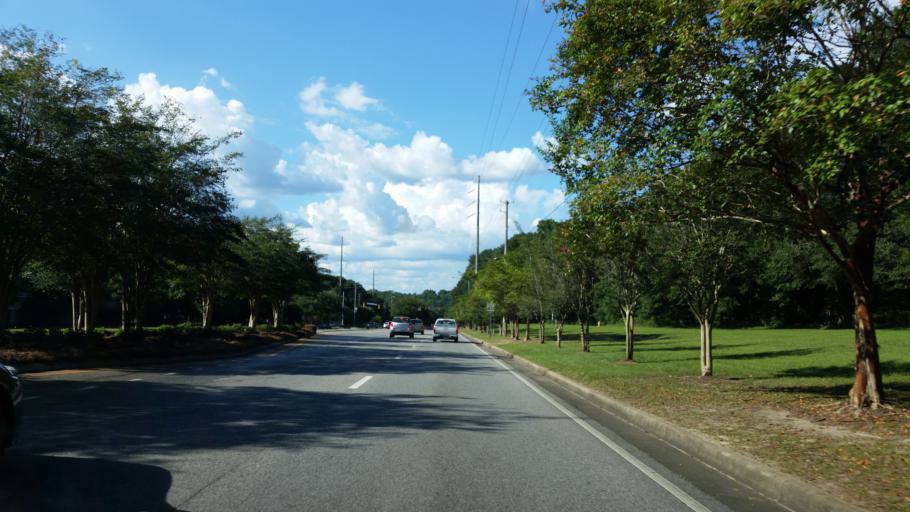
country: US
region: Alabama
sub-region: Mobile County
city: Prichard
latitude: 30.6995
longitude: -88.1740
